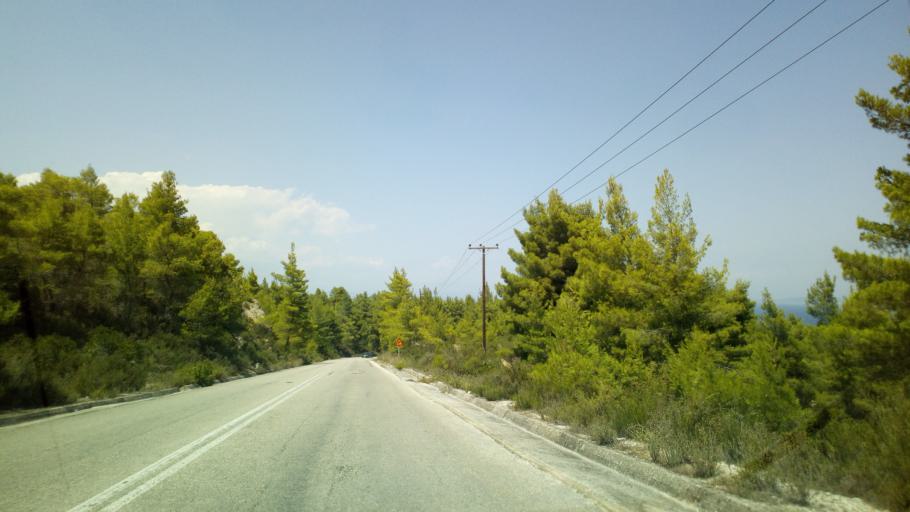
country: GR
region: Central Macedonia
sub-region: Nomos Chalkidikis
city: Sarti
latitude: 40.1399
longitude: 23.9227
